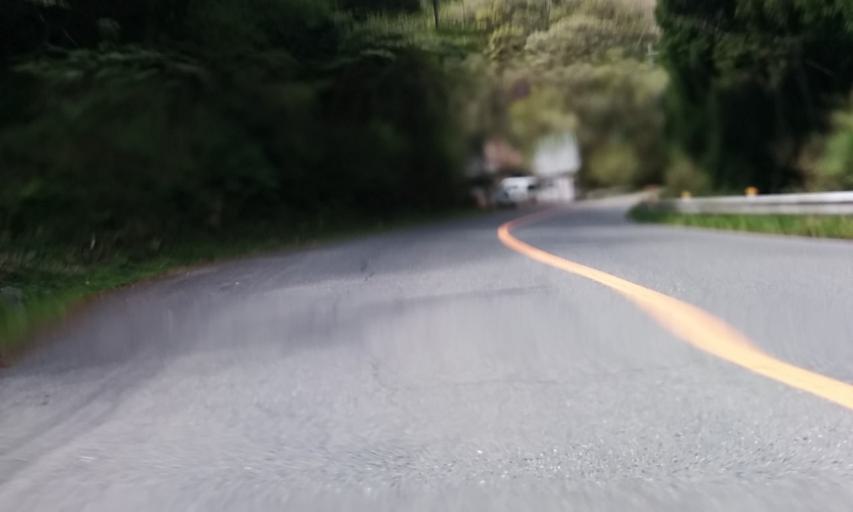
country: JP
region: Kyoto
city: Kameoka
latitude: 34.9467
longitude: 135.5940
